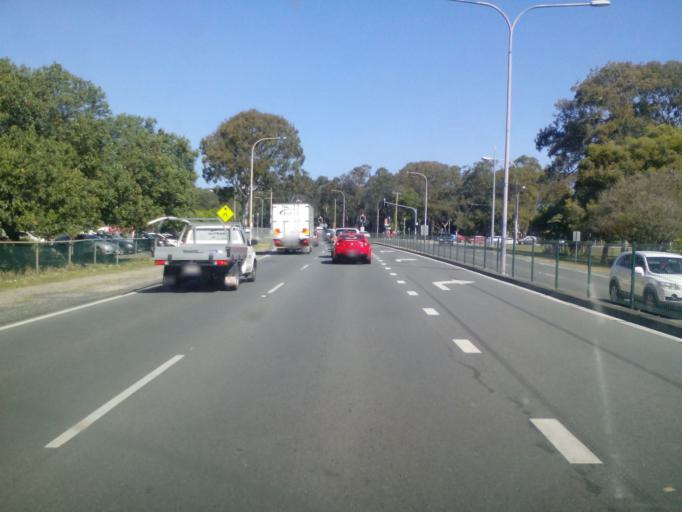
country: AU
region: Queensland
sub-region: Gold Coast
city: Palm Beach
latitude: -28.1269
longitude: 153.4763
